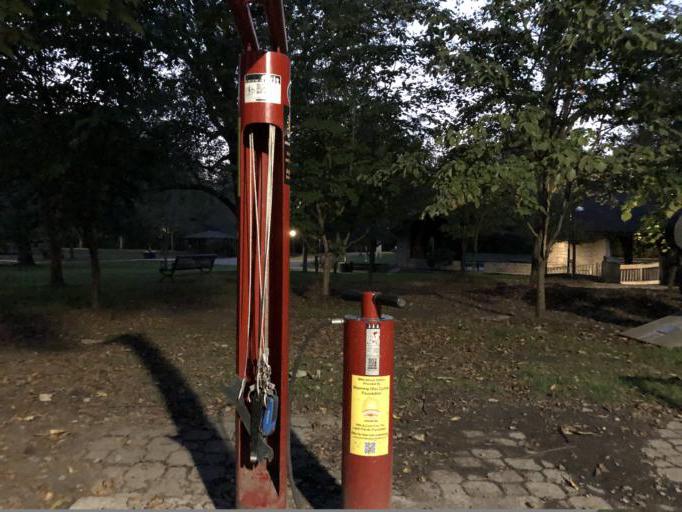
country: US
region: Ohio
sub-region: Hamilton County
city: Loveland
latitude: 39.2699
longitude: -84.2576
